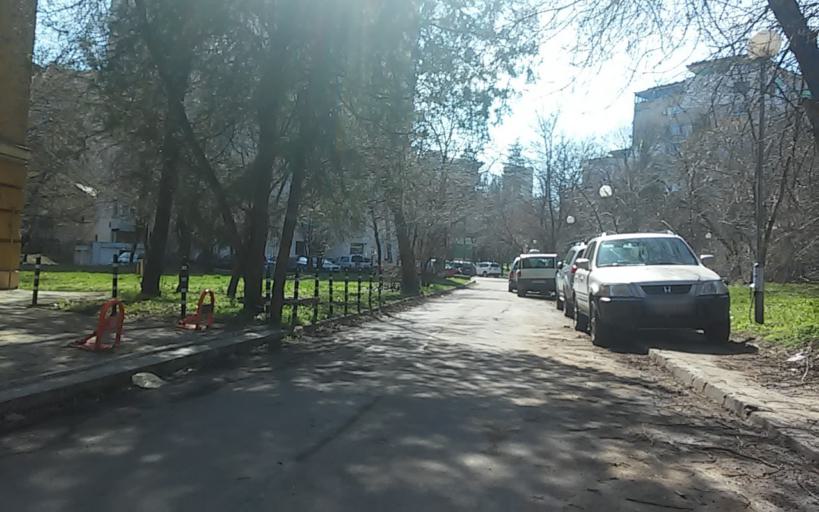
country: BG
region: Sofia-Capital
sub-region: Stolichna Obshtina
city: Sofia
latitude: 42.6773
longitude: 23.3542
